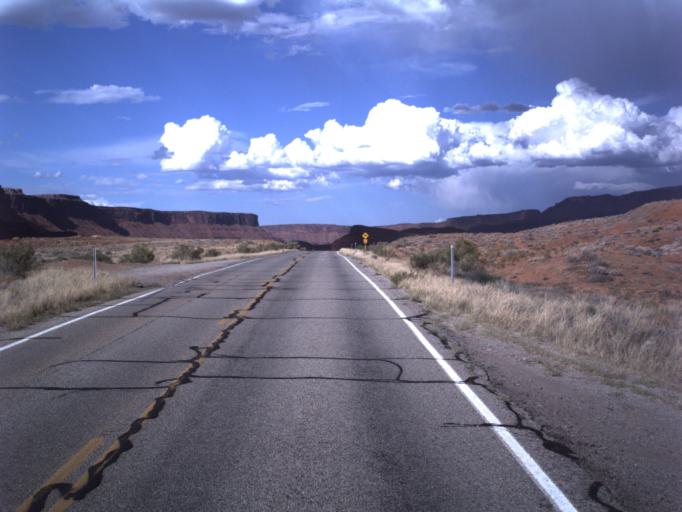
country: US
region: Utah
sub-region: Grand County
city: Moab
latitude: 38.6899
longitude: -109.4143
